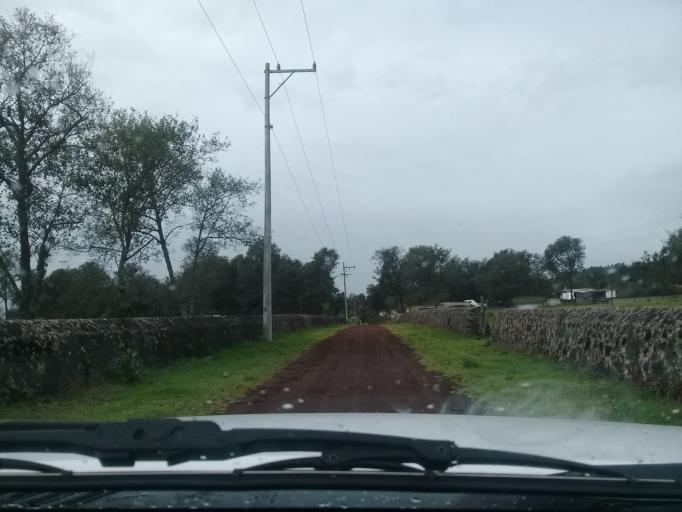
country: MX
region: Veracruz
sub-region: Acajete
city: La Joya
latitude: 19.6220
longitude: -97.0006
